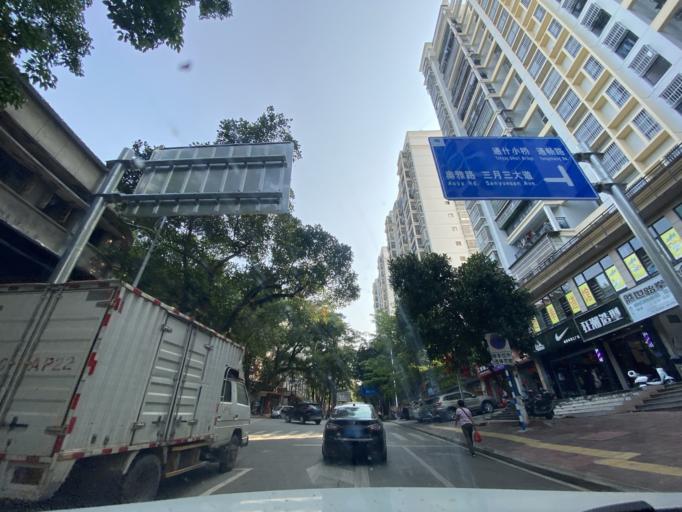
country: CN
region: Hainan
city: Chongshan
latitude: 18.7793
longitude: 109.5107
